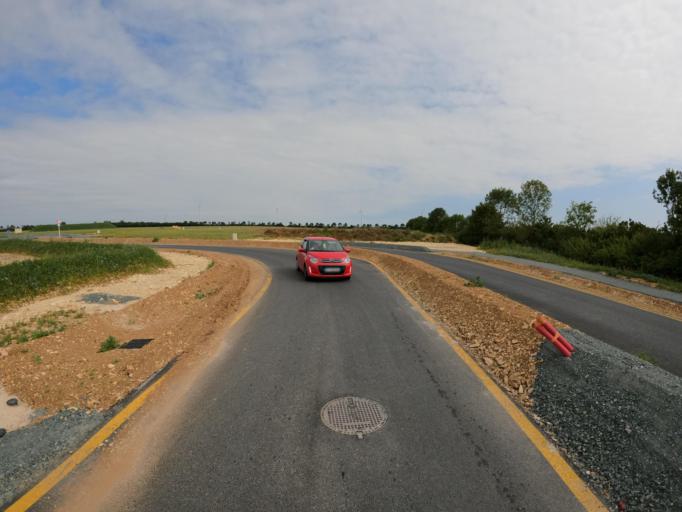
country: FR
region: Poitou-Charentes
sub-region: Departement de la Charente-Maritime
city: Saint-Jean-de-Liversay
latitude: 46.2291
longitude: -0.8759
